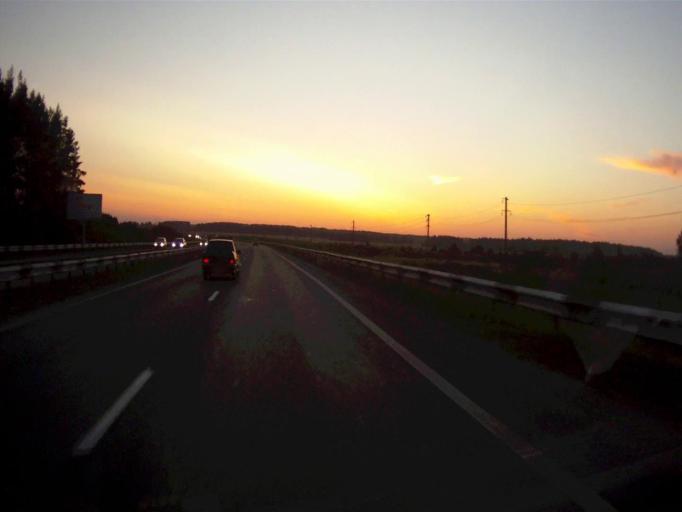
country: RU
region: Chelyabinsk
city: Roshchino
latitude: 55.1945
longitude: 61.2116
